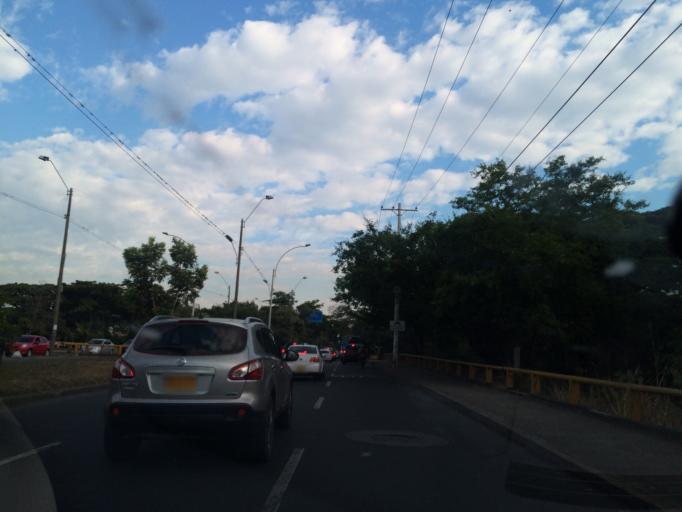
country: CO
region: Valle del Cauca
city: Cali
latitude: 3.3840
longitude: -76.5384
